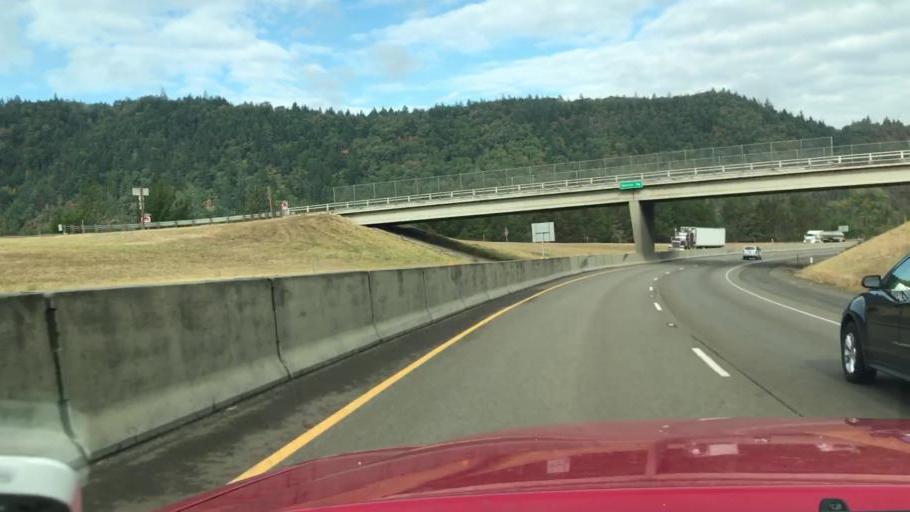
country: US
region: Oregon
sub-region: Douglas County
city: Riddle
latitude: 42.9490
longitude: -123.3284
